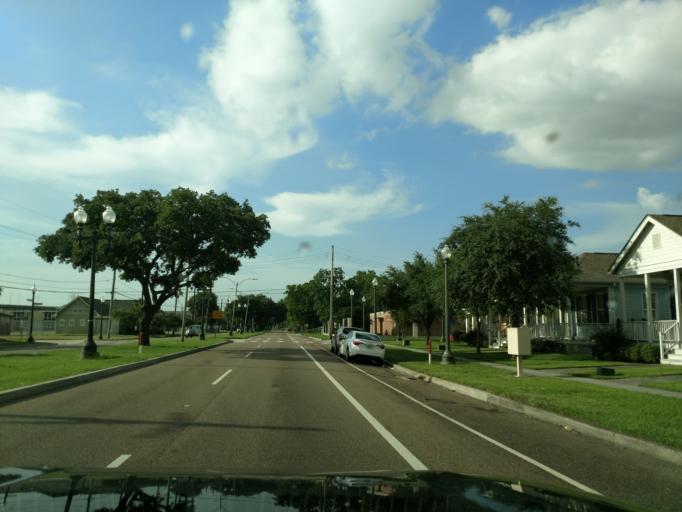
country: US
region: Louisiana
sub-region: Jefferson Parish
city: Gretna
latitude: 29.9331
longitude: -90.0416
